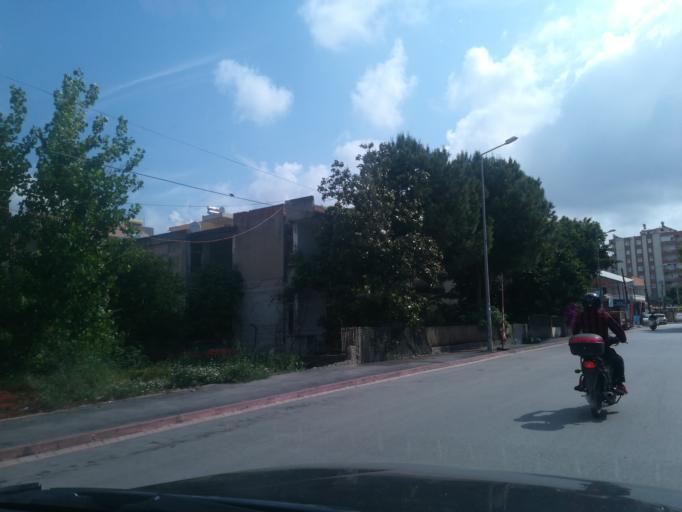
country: TR
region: Adana
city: Adana
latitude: 37.0045
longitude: 35.3132
